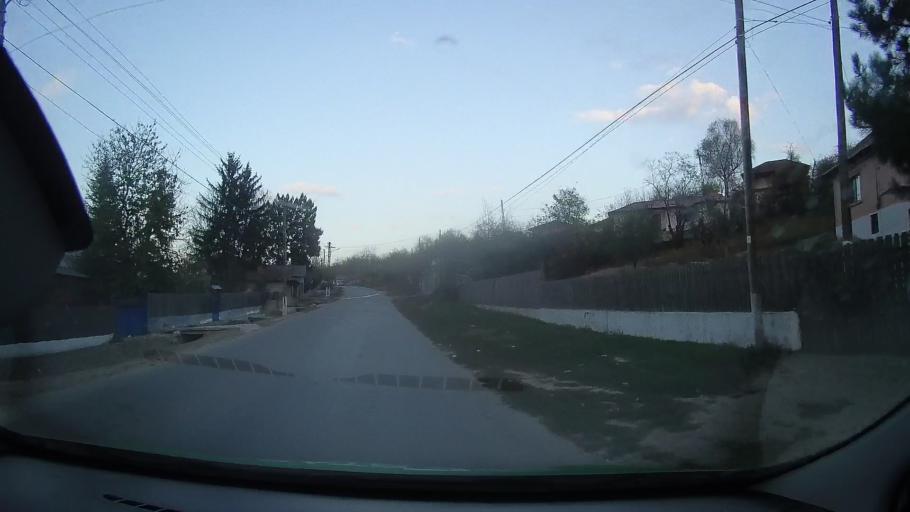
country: RO
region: Constanta
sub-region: Comuna Lipnita
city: Lipnita
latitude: 44.0938
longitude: 27.6059
